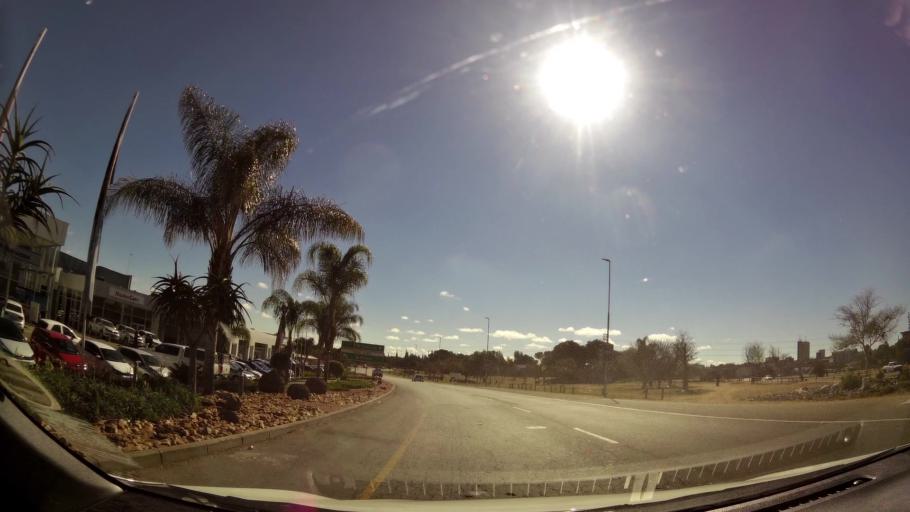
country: ZA
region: Limpopo
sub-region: Capricorn District Municipality
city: Polokwane
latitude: -23.9139
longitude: 29.4447
